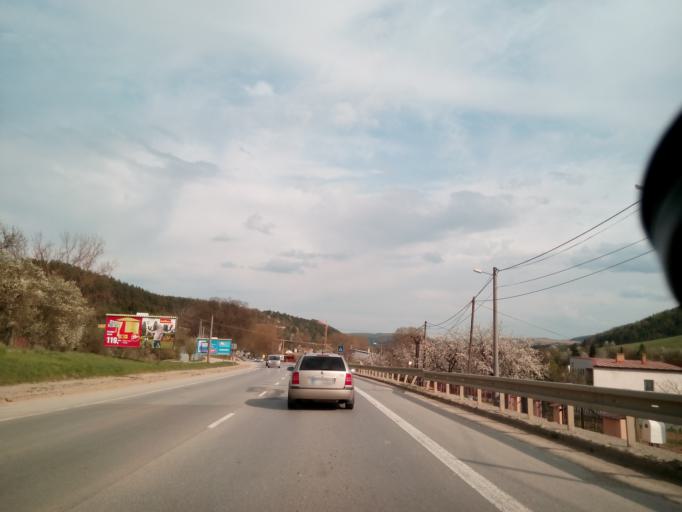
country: SK
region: Presovsky
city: Sabinov
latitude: 49.0215
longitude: 21.0278
